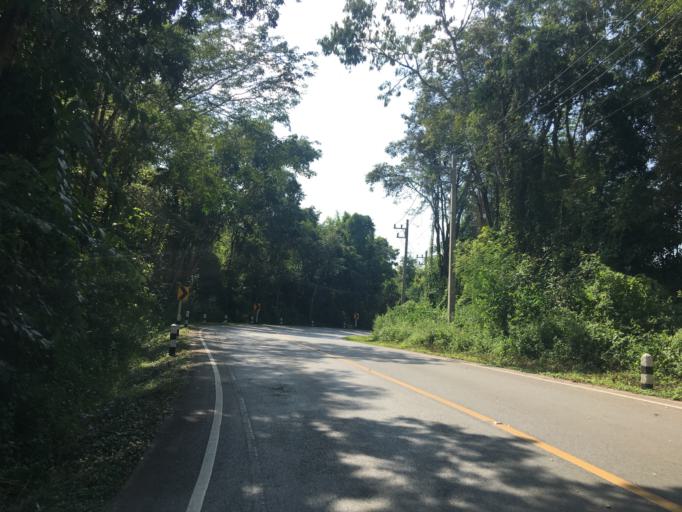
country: TH
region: Nan
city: Ban Luang
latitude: 18.8443
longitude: 100.4122
